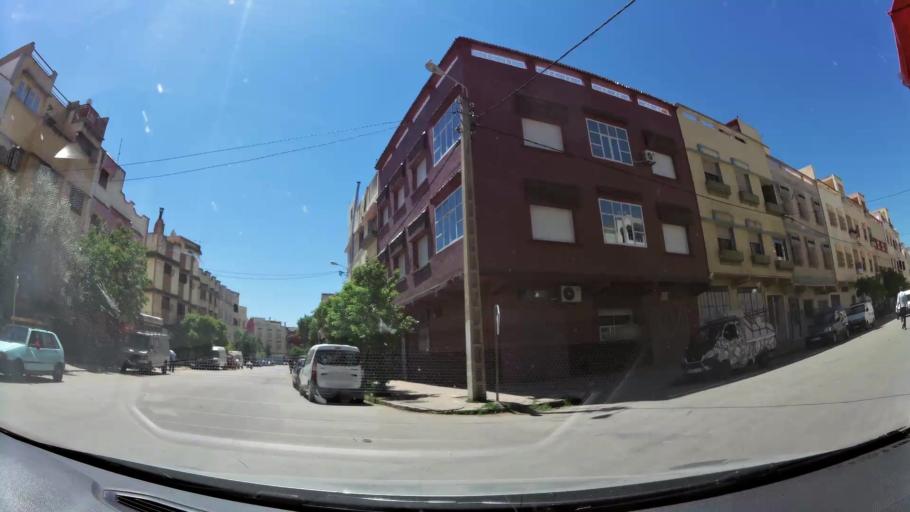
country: MA
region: Meknes-Tafilalet
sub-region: Meknes
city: Meknes
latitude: 33.8948
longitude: -5.5799
